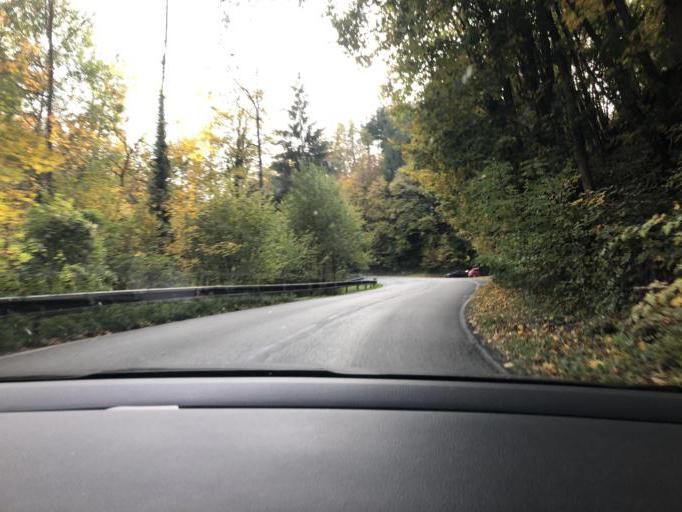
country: CZ
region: Central Bohemia
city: Divisov
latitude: 49.8086
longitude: 14.9250
